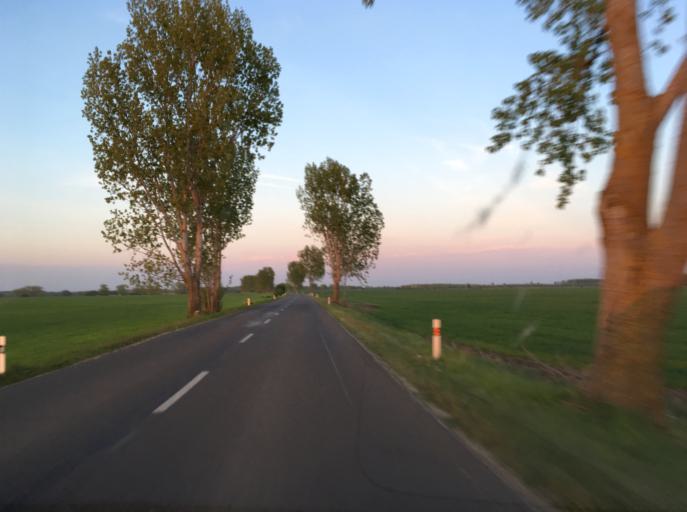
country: SK
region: Nitriansky
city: Kolarovo
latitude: 47.9189
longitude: 18.0780
